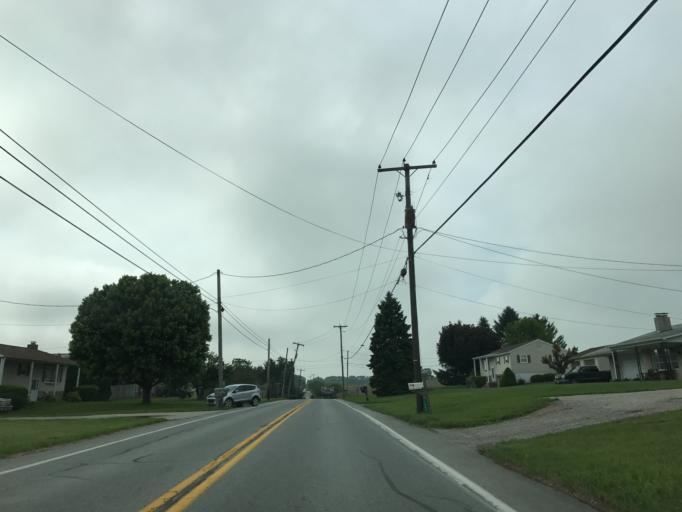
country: US
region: Pennsylvania
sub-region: York County
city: Windsor
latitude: 39.8825
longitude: -76.5392
